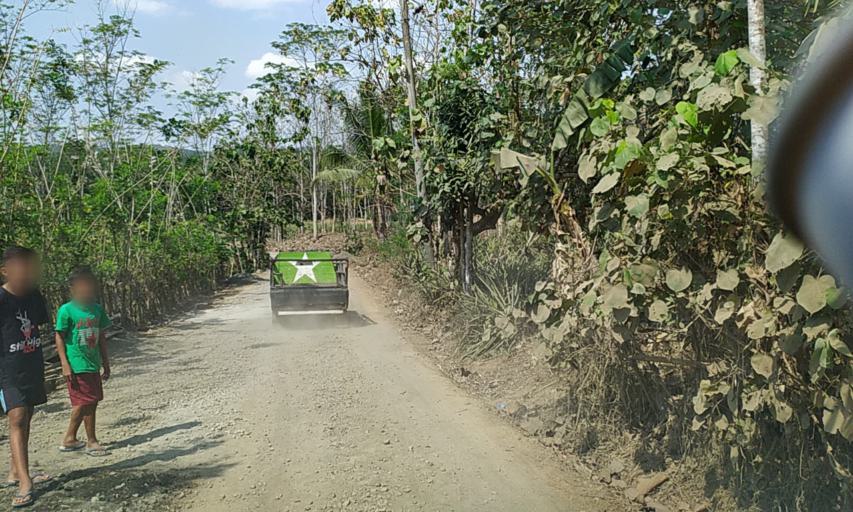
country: ID
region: Central Java
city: Cidadap
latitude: -7.4028
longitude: 108.8450
